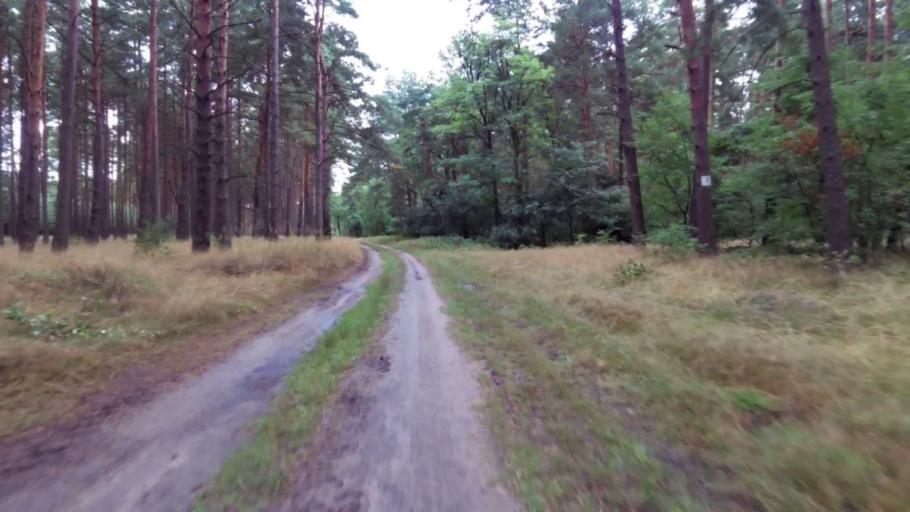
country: PL
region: West Pomeranian Voivodeship
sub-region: Powiat mysliborski
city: Debno
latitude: 52.8264
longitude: 14.6762
